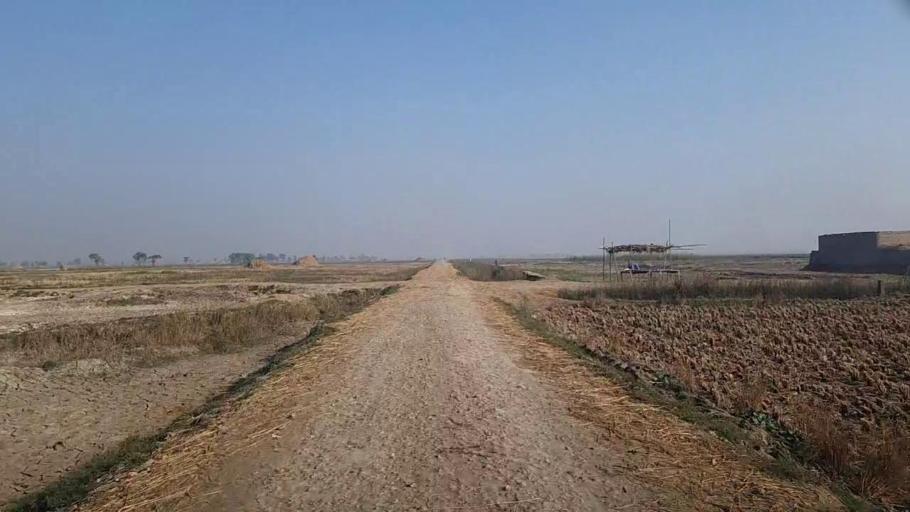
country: PK
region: Sindh
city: Radhan
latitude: 27.1346
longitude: 67.9046
